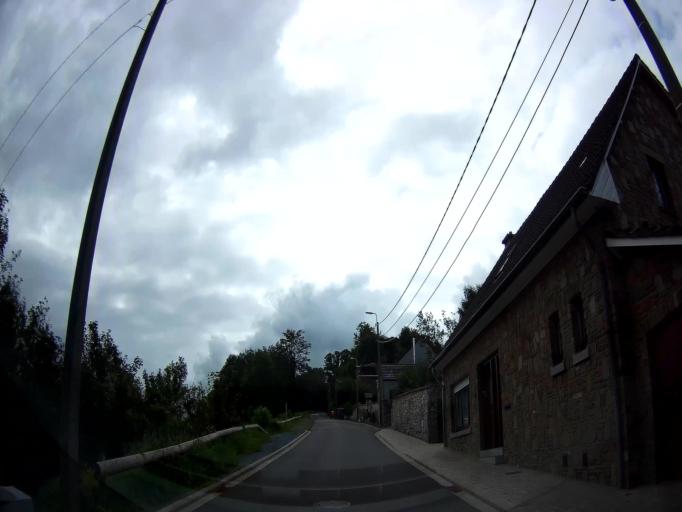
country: BE
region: Wallonia
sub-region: Province de Liege
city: Limbourg
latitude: 50.6161
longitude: 5.9410
